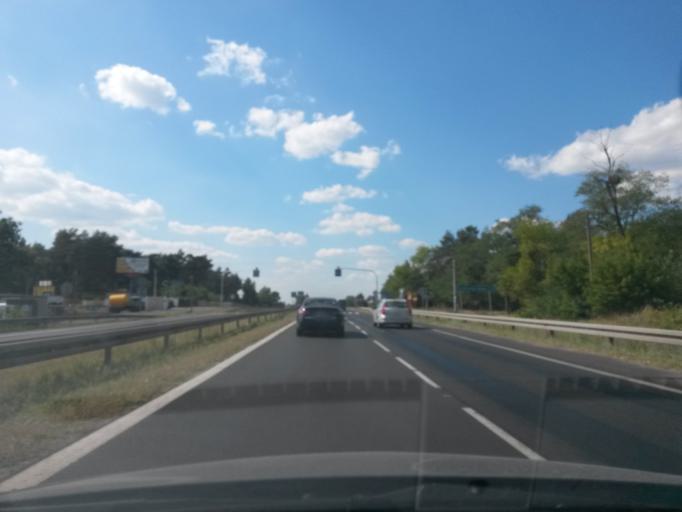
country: PL
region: Masovian Voivodeship
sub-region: Powiat warszawski zachodni
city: Dziekanow Lesny
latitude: 52.3631
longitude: 20.8182
